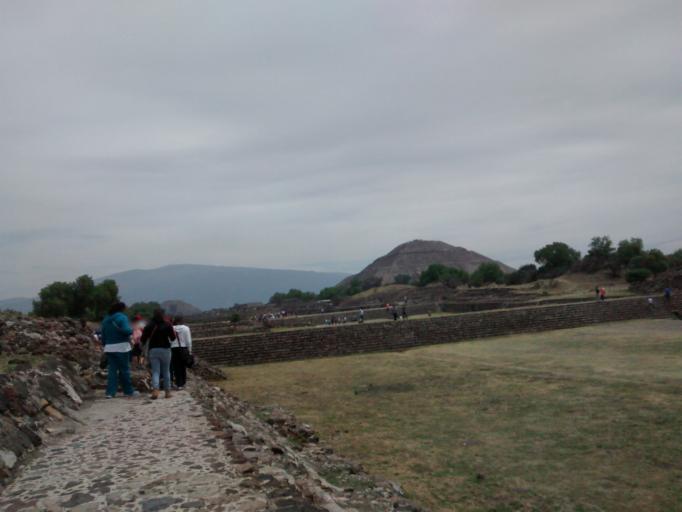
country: MX
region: Mexico
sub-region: Teotihuacan
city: Teotihuacan de Arista
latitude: 19.6874
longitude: -98.8479
